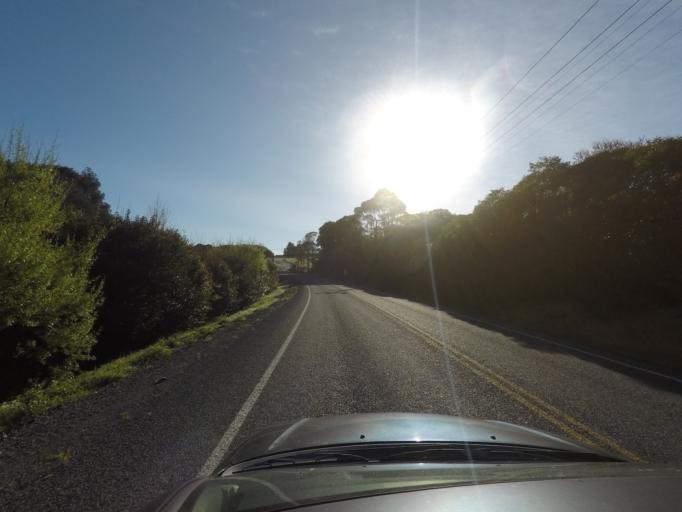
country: NZ
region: Auckland
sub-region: Auckland
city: Red Hill
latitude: -36.9958
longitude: 174.9826
